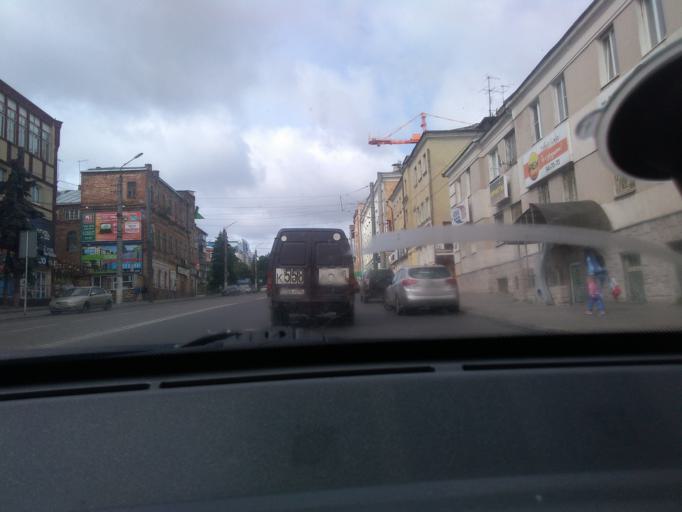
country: RU
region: Kursk
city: Kursk
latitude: 51.7259
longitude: 36.1816
